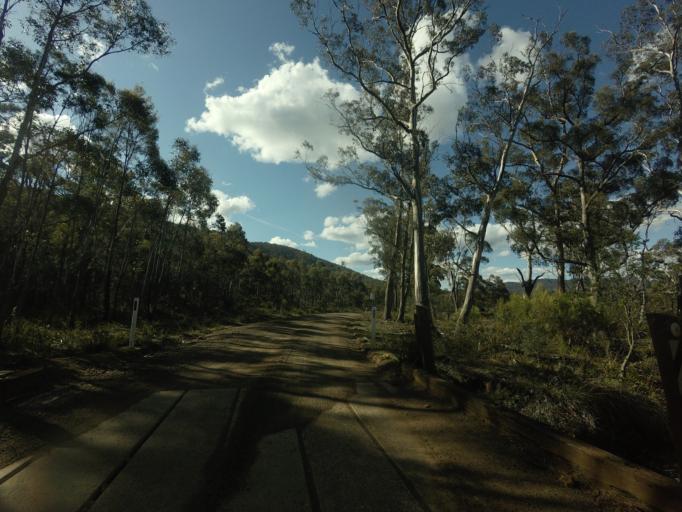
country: AU
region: Tasmania
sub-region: Break O'Day
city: St Helens
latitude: -41.8509
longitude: 148.0109
